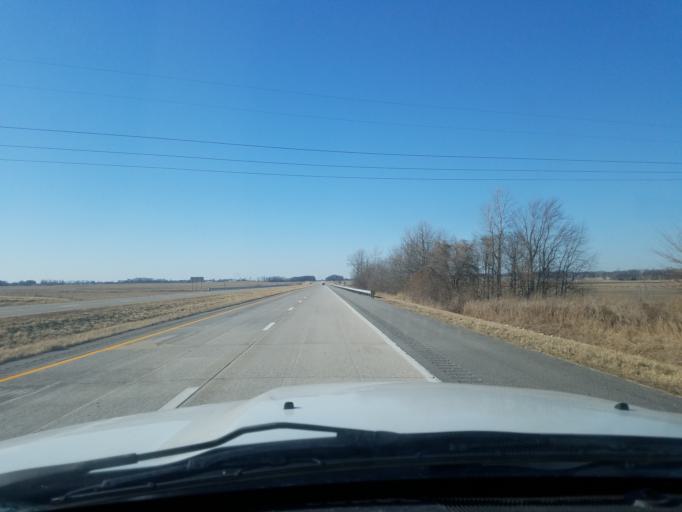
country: US
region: Kentucky
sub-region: Henderson County
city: Henderson
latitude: 37.7991
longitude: -87.5101
